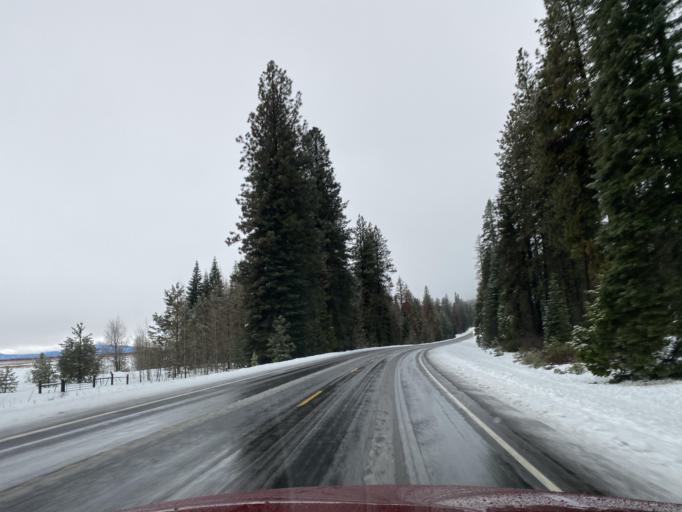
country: US
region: Oregon
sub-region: Klamath County
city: Klamath Falls
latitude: 42.5487
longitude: -122.0863
